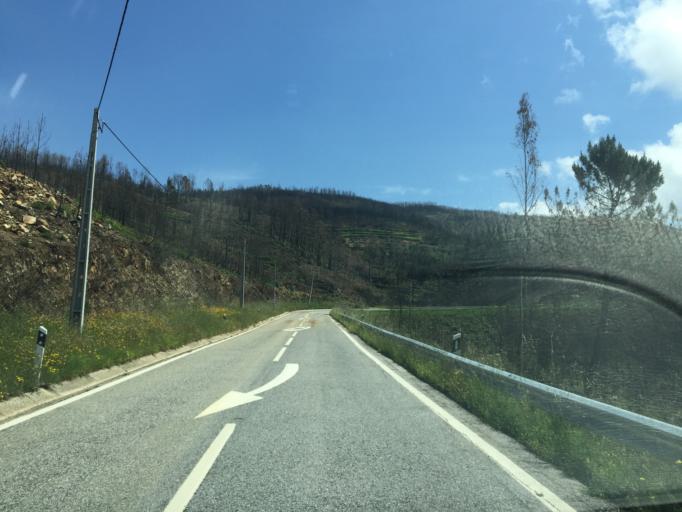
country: PT
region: Castelo Branco
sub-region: Oleiros
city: Oleiros
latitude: 39.9699
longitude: -7.9570
